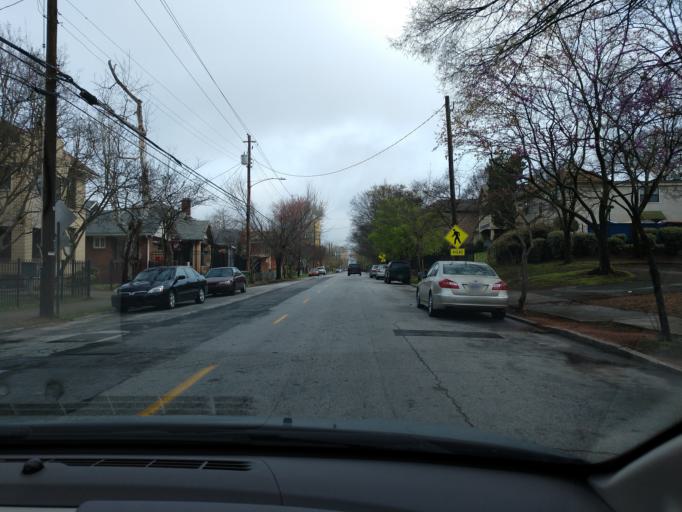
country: US
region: Georgia
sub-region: Fulton County
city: Atlanta
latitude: 33.7651
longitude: -84.3735
